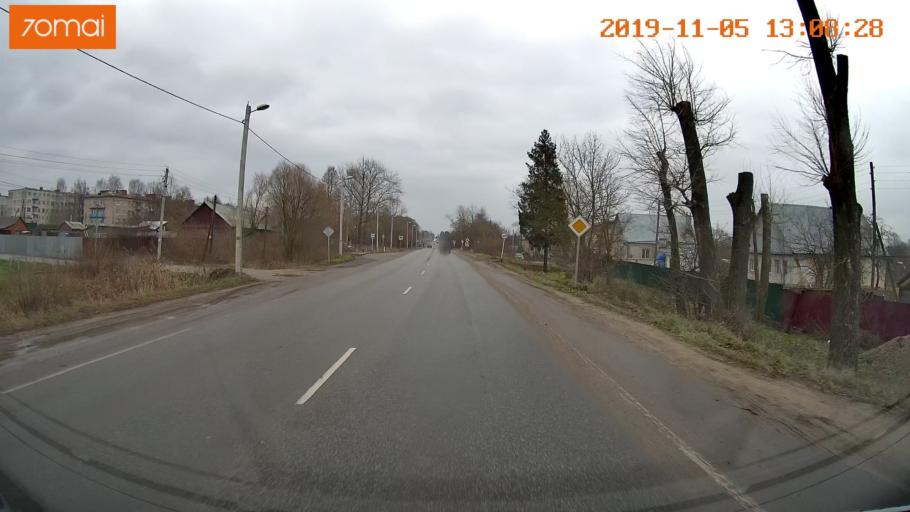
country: RU
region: Ivanovo
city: Kitovo
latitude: 56.8643
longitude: 41.2910
